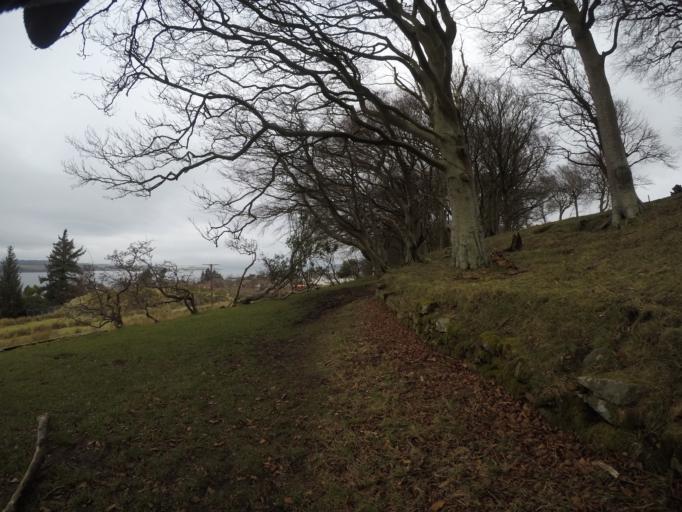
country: GB
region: Scotland
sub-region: North Ayrshire
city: Fairlie
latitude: 55.7562
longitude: -4.8496
